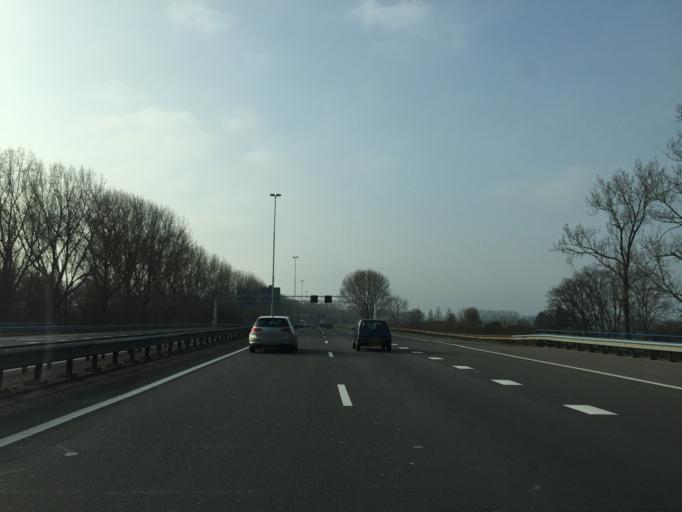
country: NL
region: South Holland
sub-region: Gemeente Maassluis
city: Maassluis
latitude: 51.9258
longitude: 4.2663
